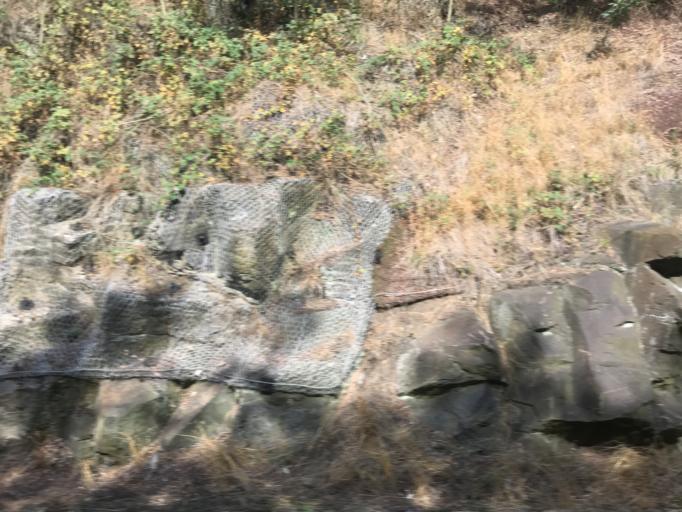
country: CZ
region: Central Bohemia
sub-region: Okres Benesov
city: Cercany
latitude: 49.8370
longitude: 14.6997
